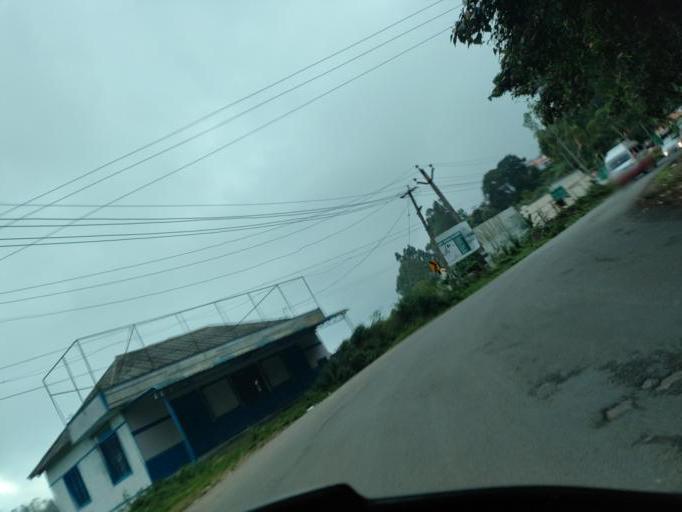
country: IN
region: Tamil Nadu
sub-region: Dindigul
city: Kodaikanal
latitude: 10.2328
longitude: 77.5037
